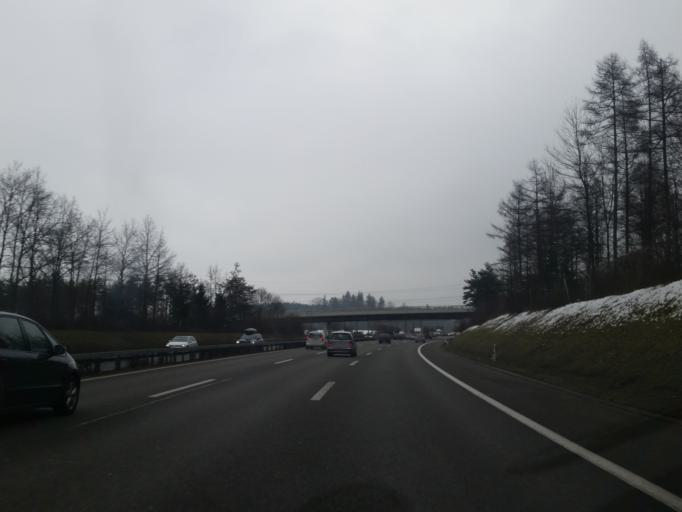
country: CH
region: Zurich
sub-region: Bezirk Pfaeffikon
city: Tagelswangen
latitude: 47.4363
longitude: 8.6818
